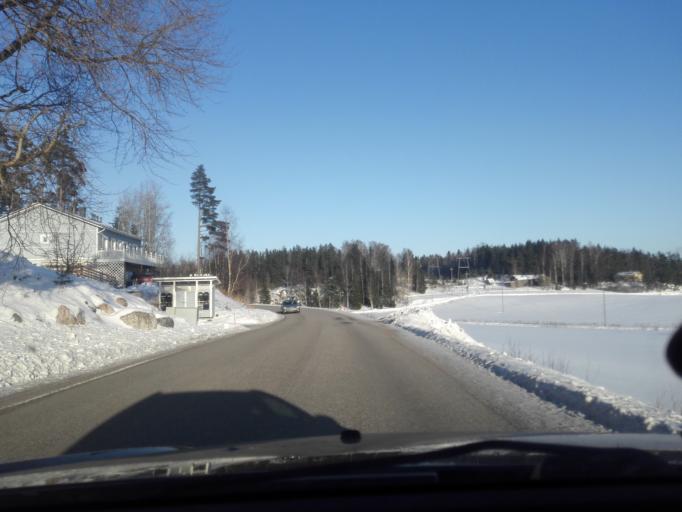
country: FI
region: Uusimaa
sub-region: Helsinki
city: Kerava
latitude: 60.3396
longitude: 25.1514
